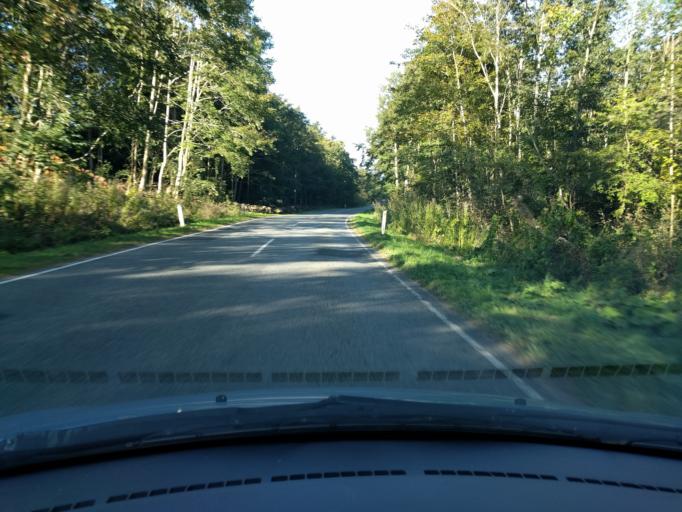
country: DK
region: South Denmark
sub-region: Assens Kommune
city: Assens
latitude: 55.2160
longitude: 9.9969
